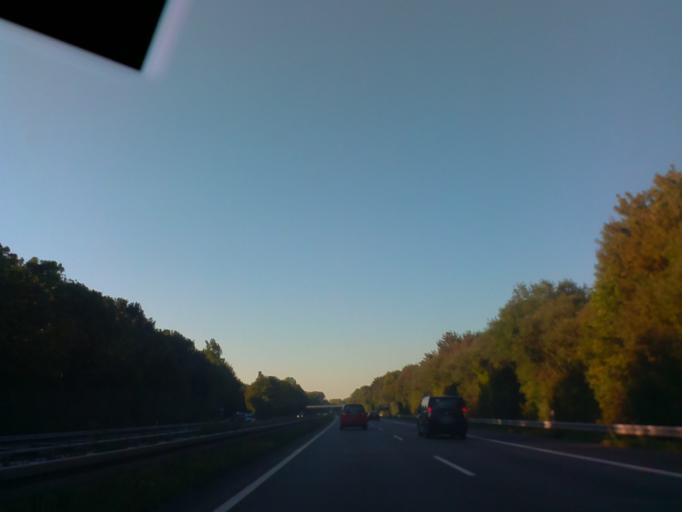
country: DE
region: Hesse
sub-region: Regierungsbezirk Darmstadt
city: Heppenheim an der Bergstrasse
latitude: 49.6188
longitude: 8.6229
